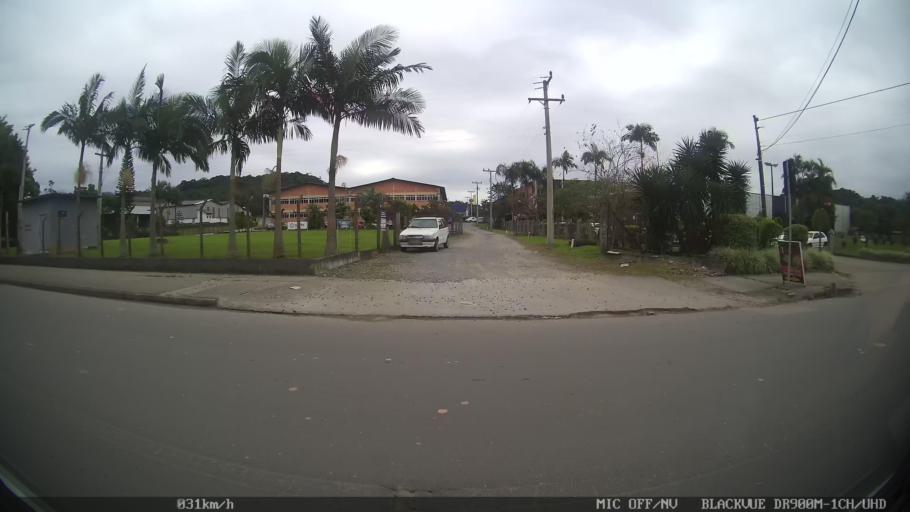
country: BR
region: Santa Catarina
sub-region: Joinville
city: Joinville
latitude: -26.2643
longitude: -48.8851
